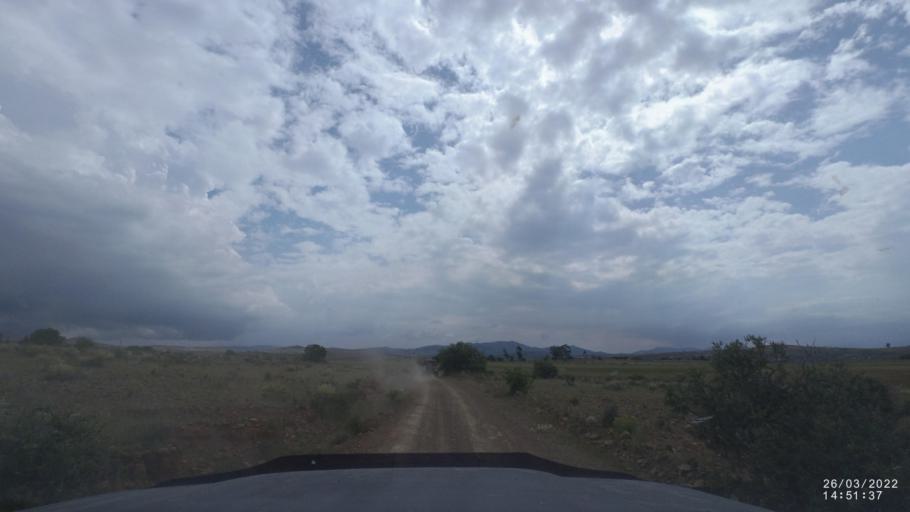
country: BO
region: Cochabamba
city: Cliza
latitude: -17.7260
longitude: -65.8540
